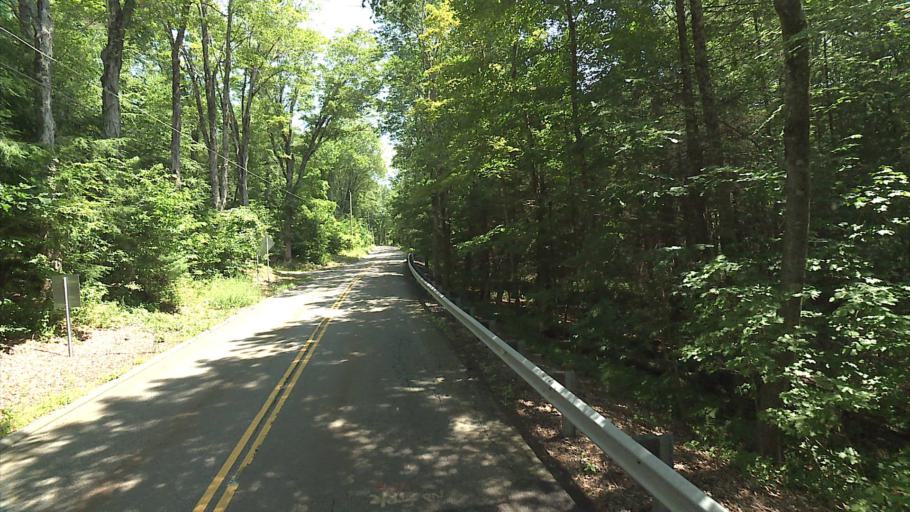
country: US
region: Connecticut
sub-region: Litchfield County
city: Winchester Center
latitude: 41.9015
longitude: -73.1705
